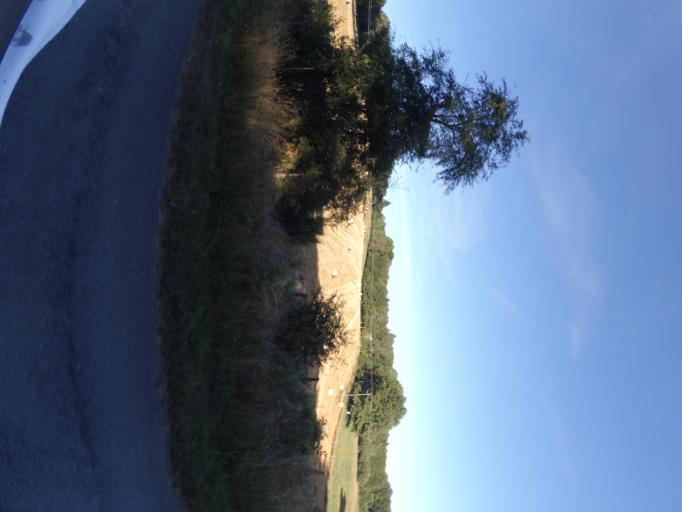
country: FR
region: Limousin
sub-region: Departement de la Creuse
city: Banize
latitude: 45.7254
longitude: 2.0417
